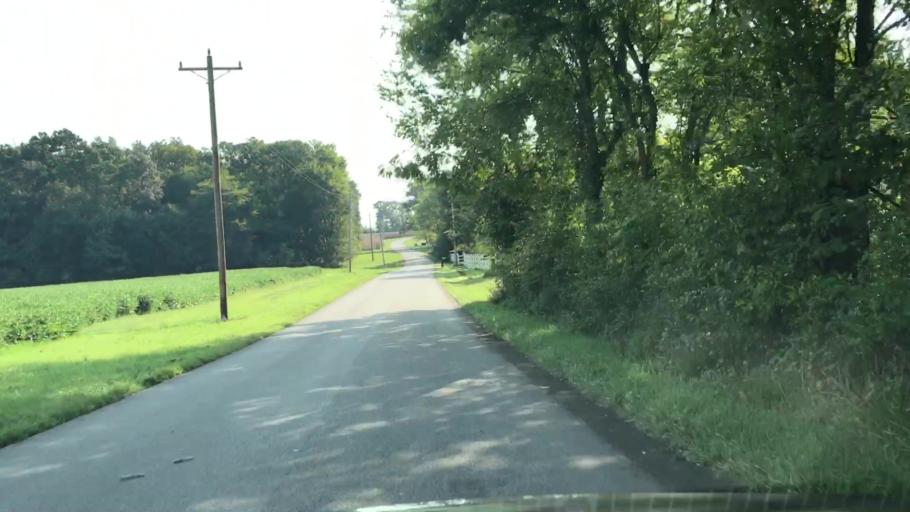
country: US
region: Kentucky
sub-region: Todd County
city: Elkton
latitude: 36.7665
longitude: -87.1633
